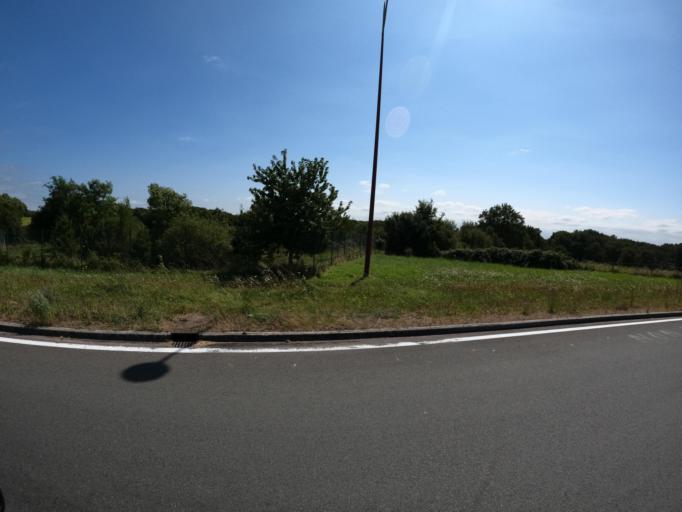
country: FR
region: Poitou-Charentes
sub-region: Departement de la Vienne
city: Charroux
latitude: 46.1412
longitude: 0.4198
